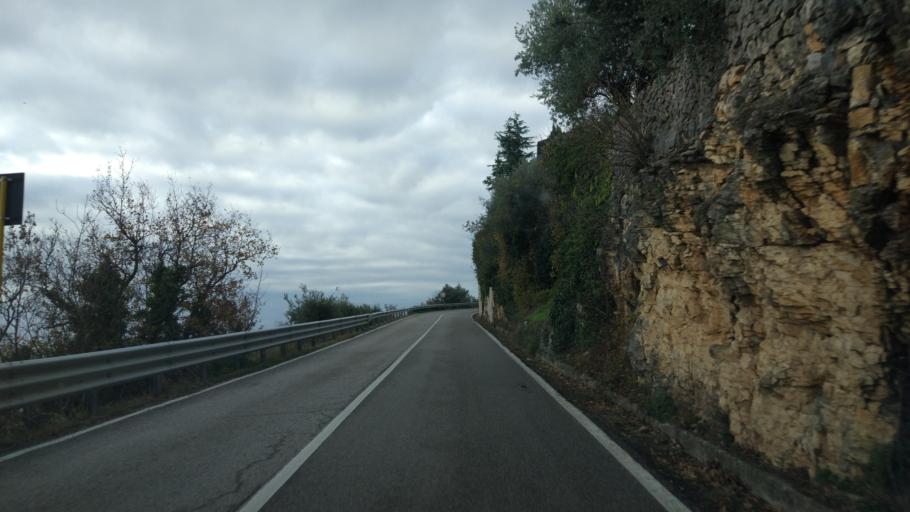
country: IT
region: Veneto
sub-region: Provincia di Verona
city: Marano di Valpolicella
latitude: 45.5531
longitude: 10.9113
